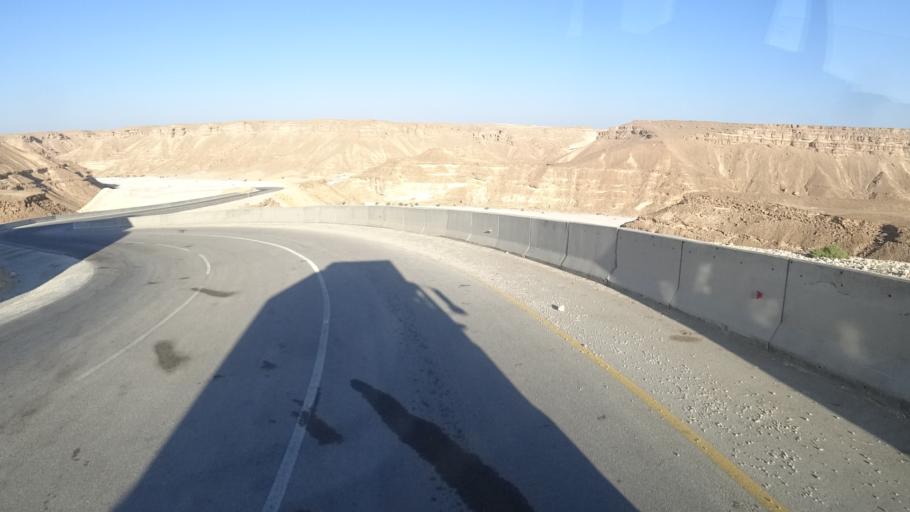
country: YE
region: Al Mahrah
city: Hawf
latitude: 17.0928
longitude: 53.0435
